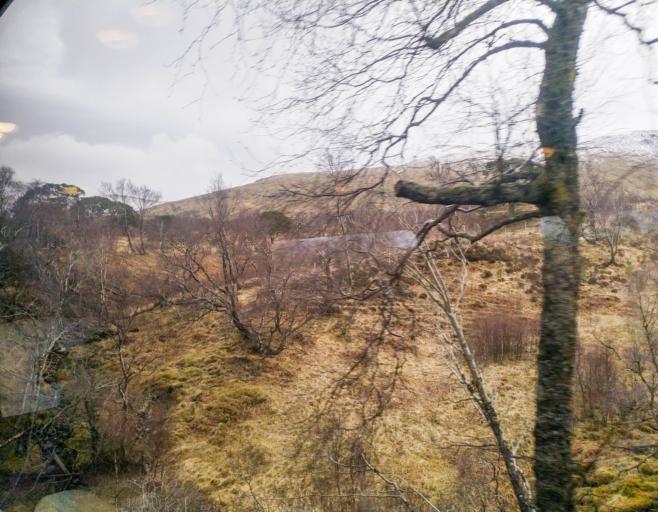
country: GB
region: Scotland
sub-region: Highland
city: Spean Bridge
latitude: 56.5707
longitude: -4.6911
